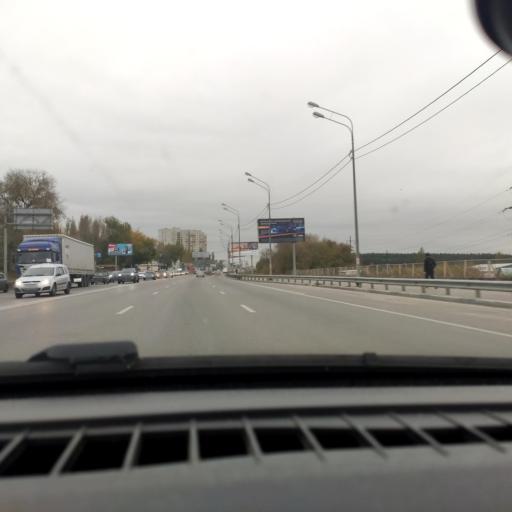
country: RU
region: Voronezj
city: Podgornoye
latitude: 51.7022
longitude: 39.1343
